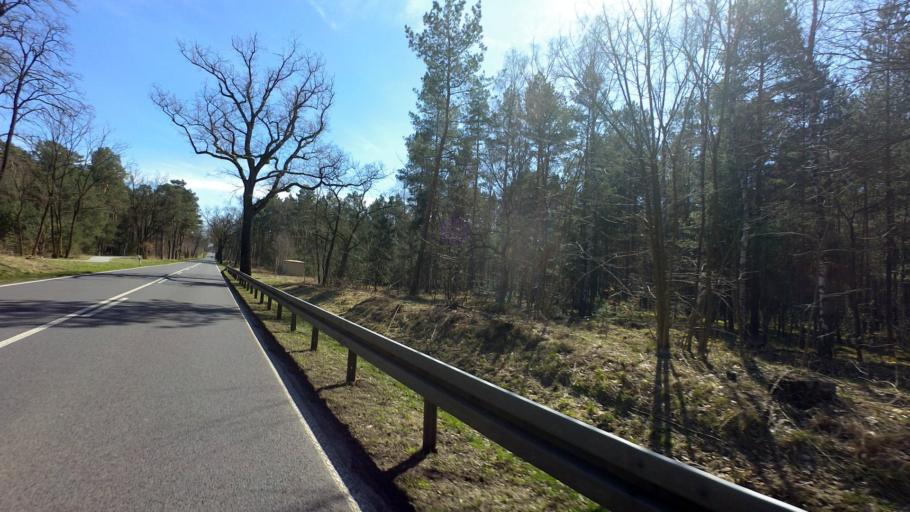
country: DE
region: Brandenburg
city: Storkow
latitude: 52.2269
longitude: 13.9692
